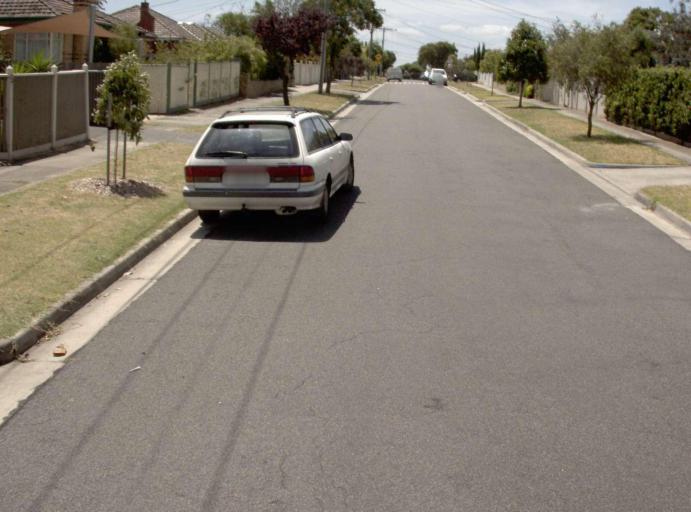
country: AU
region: Victoria
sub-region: Kingston
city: Parkdale
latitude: -37.9847
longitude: 145.0780
